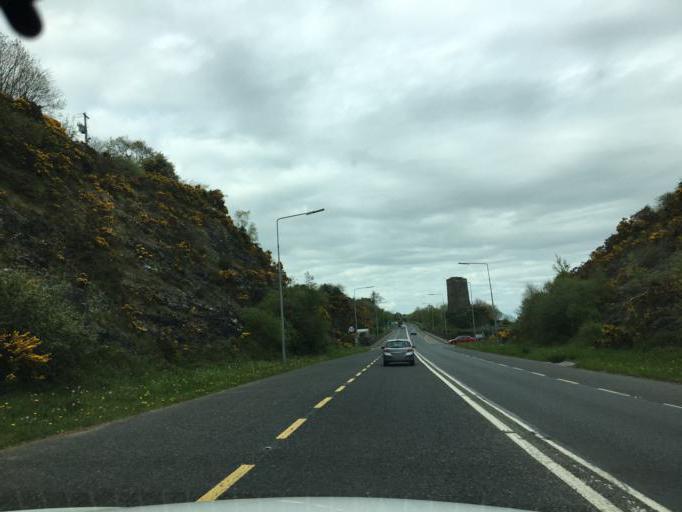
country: IE
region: Leinster
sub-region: Loch Garman
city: Loch Garman
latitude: 52.3500
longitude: -6.5124
